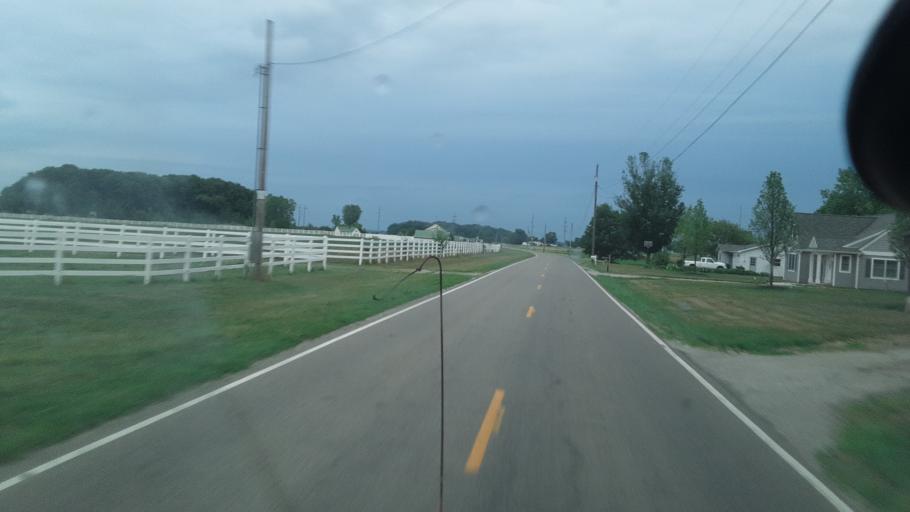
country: US
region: Ohio
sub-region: Defiance County
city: Hicksville
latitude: 41.2871
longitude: -84.7546
